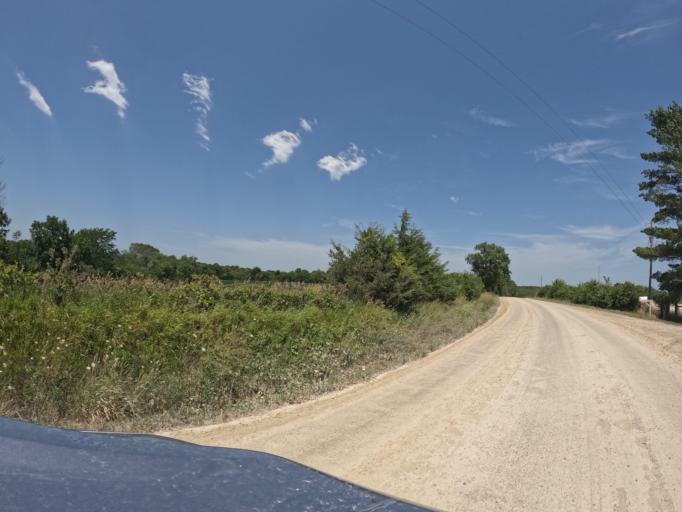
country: US
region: Iowa
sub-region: Henry County
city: Mount Pleasant
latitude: 40.9527
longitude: -91.5978
